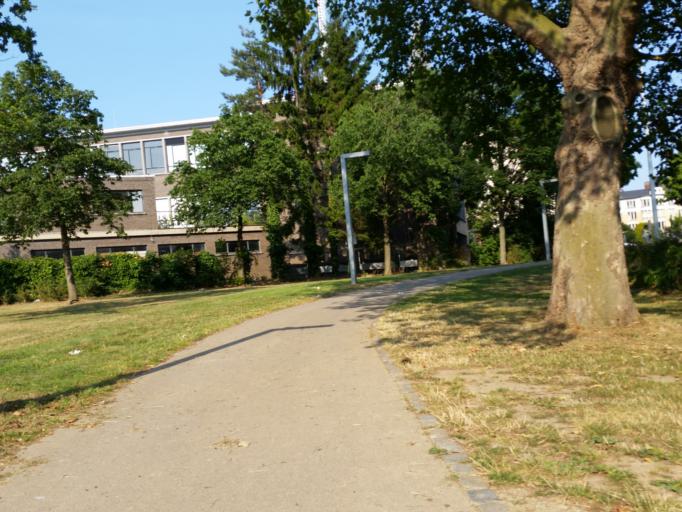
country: BE
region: Flanders
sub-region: Provincie Vlaams-Brabant
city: Vilvoorde
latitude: 50.9267
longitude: 4.4230
